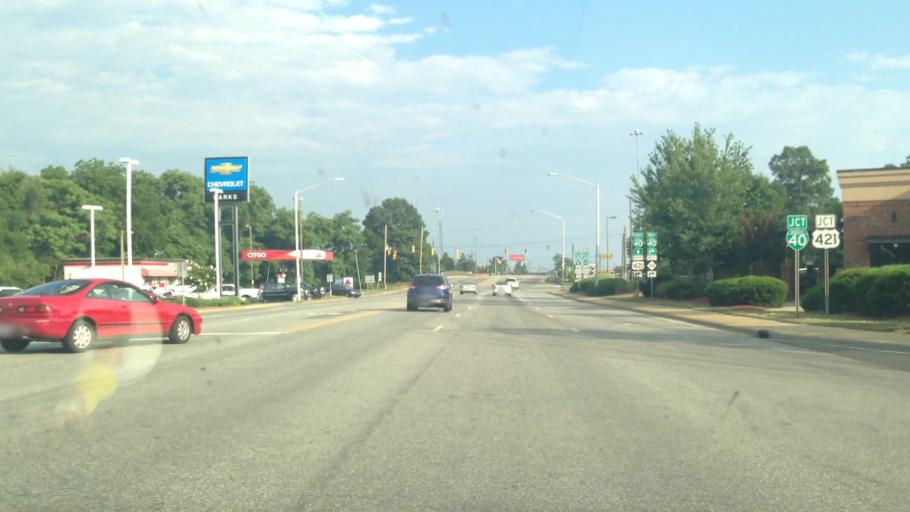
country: US
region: North Carolina
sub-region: Forsyth County
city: Kernersville
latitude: 36.1151
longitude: -80.0652
